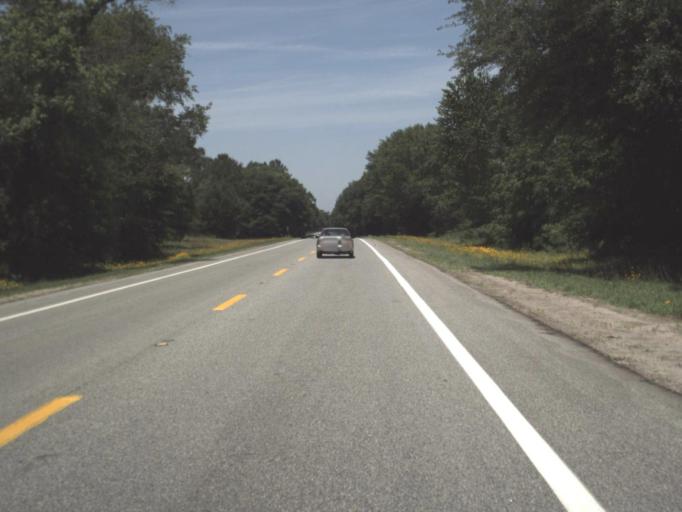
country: US
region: Florida
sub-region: Suwannee County
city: Live Oak
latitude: 30.3699
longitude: -83.1485
